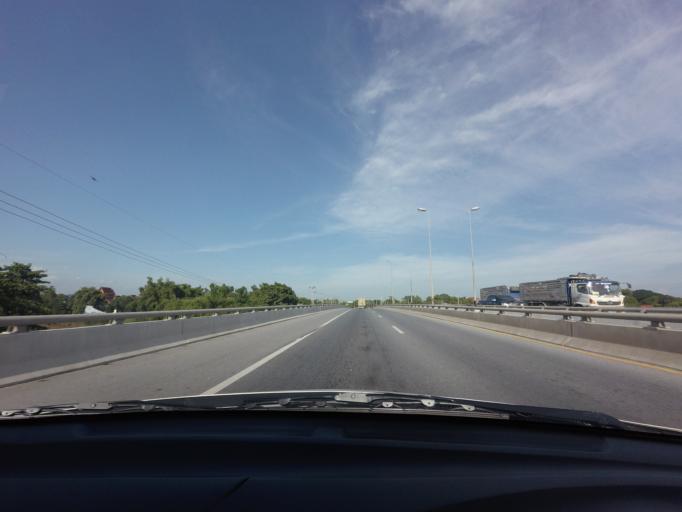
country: TH
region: Suphan Buri
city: Suphan Buri
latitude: 14.4469
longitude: 100.1187
